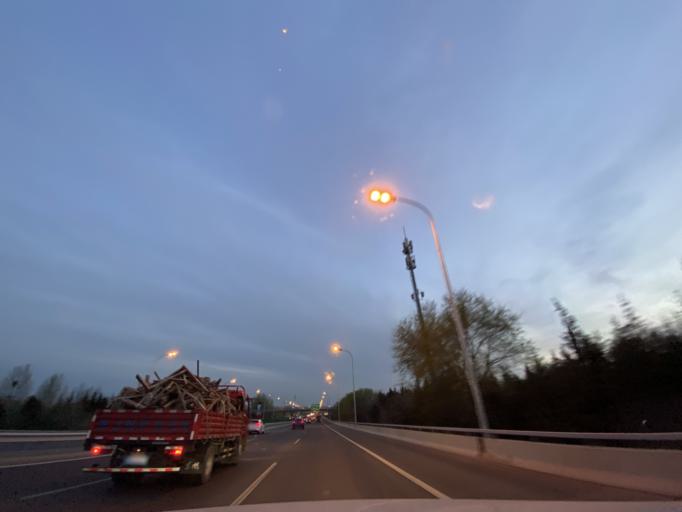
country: CN
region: Beijing
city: Xiangshan
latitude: 39.9701
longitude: 116.2133
